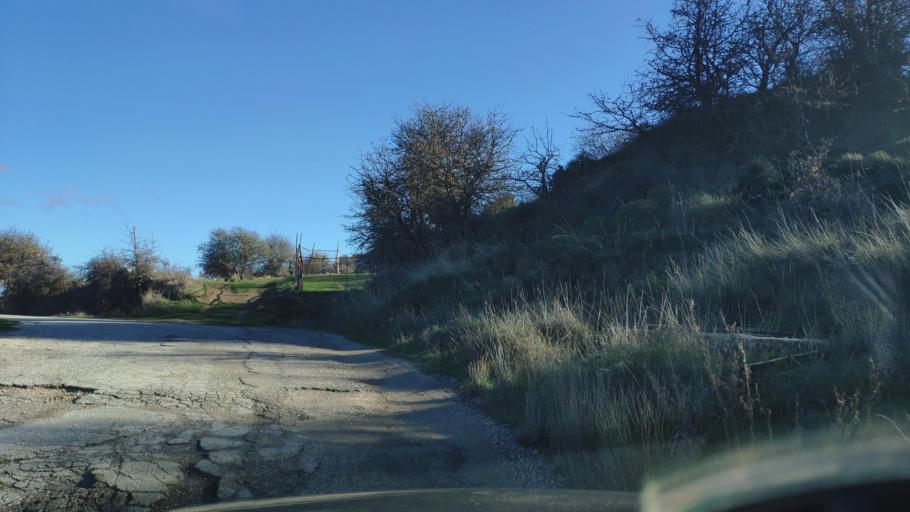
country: GR
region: West Greece
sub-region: Nomos Achaias
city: Aiyira
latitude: 38.0393
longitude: 22.4640
